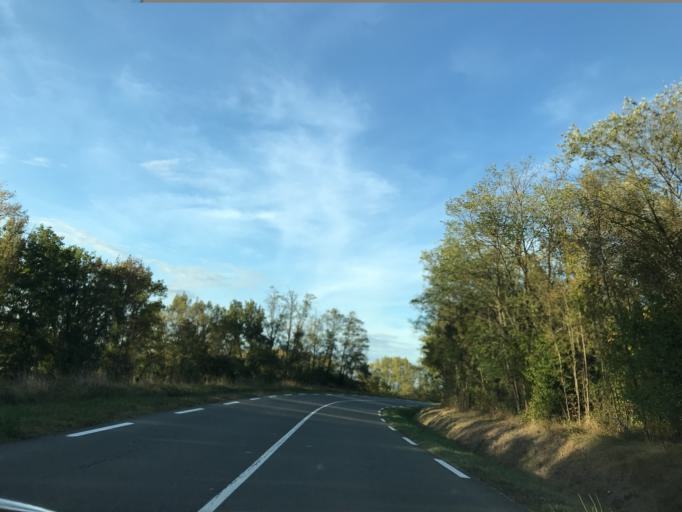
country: FR
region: Auvergne
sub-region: Departement du Puy-de-Dome
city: Puy-Guillaume
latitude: 45.9721
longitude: 3.4801
